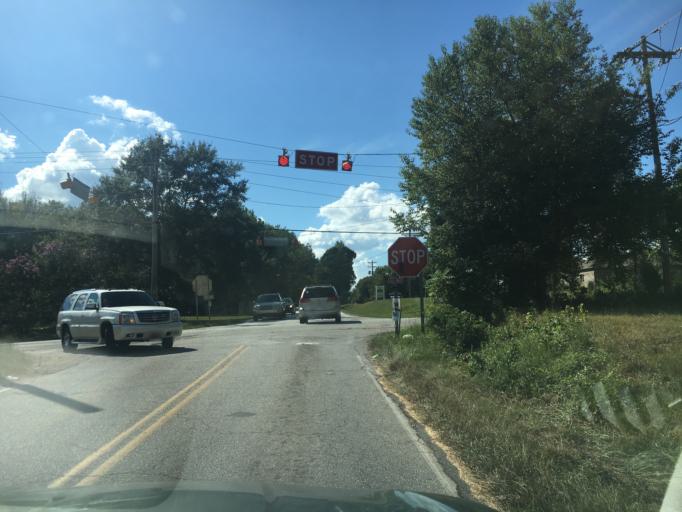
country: US
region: South Carolina
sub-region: Greenville County
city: Five Forks
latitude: 34.8225
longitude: -82.2283
